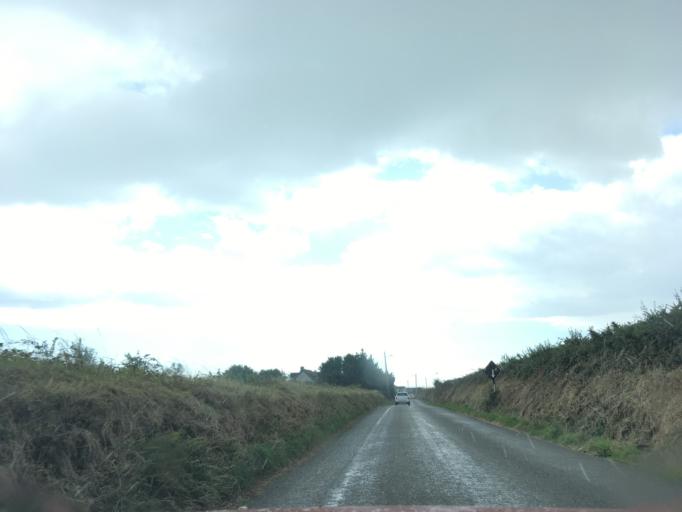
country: IE
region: Munster
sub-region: County Cork
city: Crosshaven
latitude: 51.7899
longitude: -8.3063
